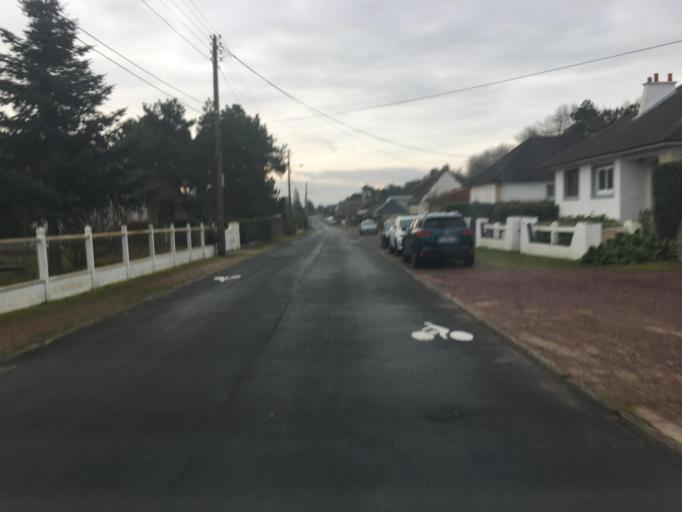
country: FR
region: Lower Normandy
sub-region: Departement du Calvados
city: Merville-Franceville-Plage
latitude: 49.2828
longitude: -0.2098
